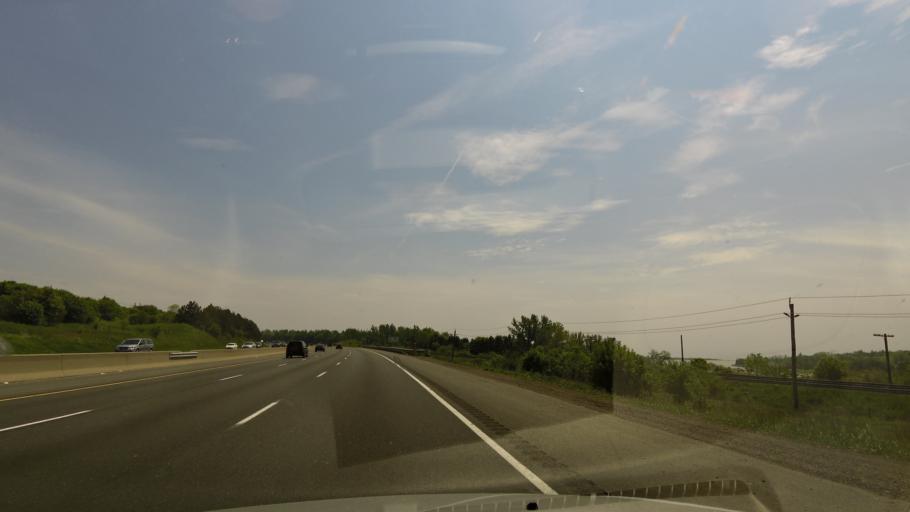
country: CA
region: Ontario
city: Oshawa
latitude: 43.8777
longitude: -78.8016
